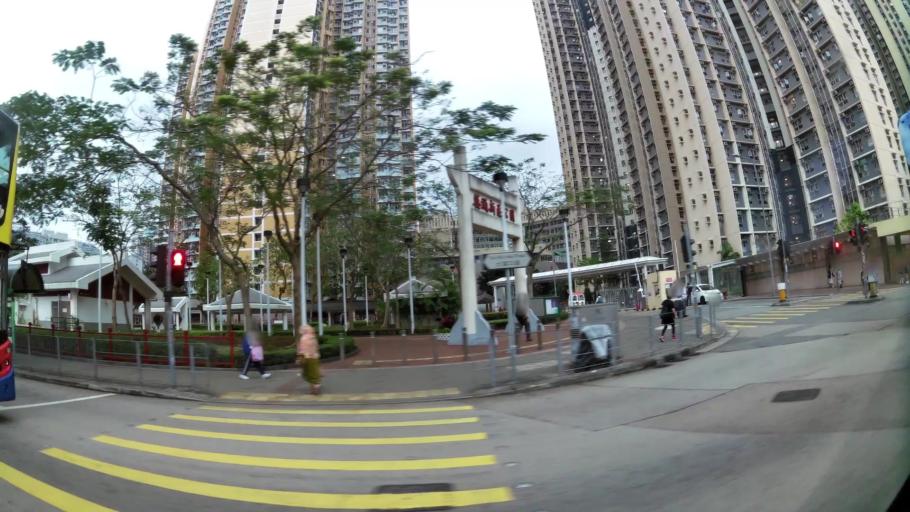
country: HK
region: Tsuen Wan
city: Tsuen Wan
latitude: 22.3681
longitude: 114.1297
